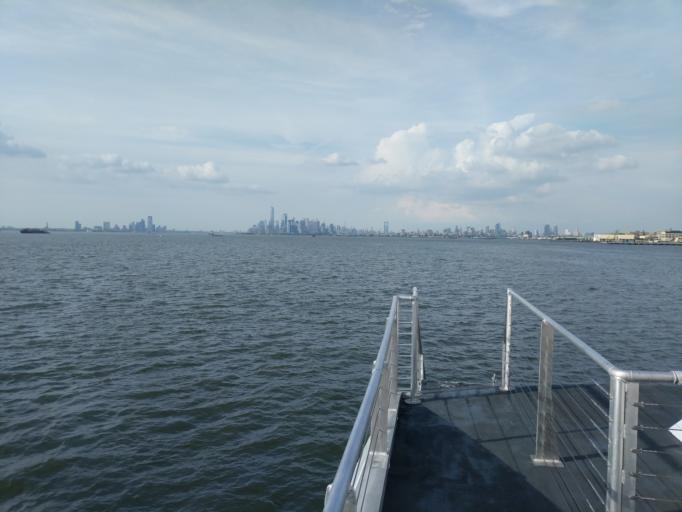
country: US
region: New York
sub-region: Kings County
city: Bensonhurst
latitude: 40.6439
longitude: -74.0368
